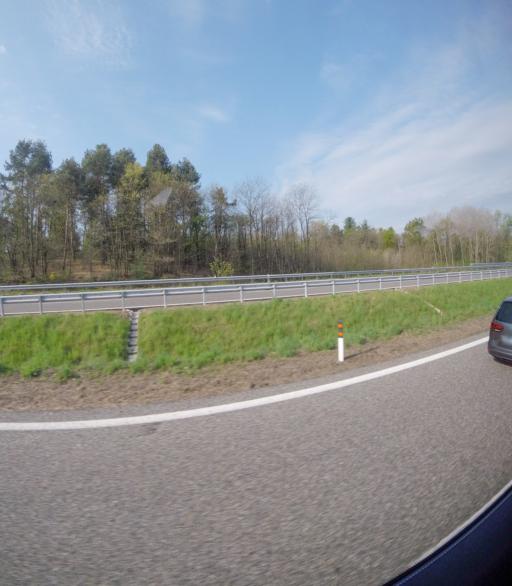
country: IT
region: Piedmont
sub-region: Provincia di Novara
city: Comignago
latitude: 45.7089
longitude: 8.5459
